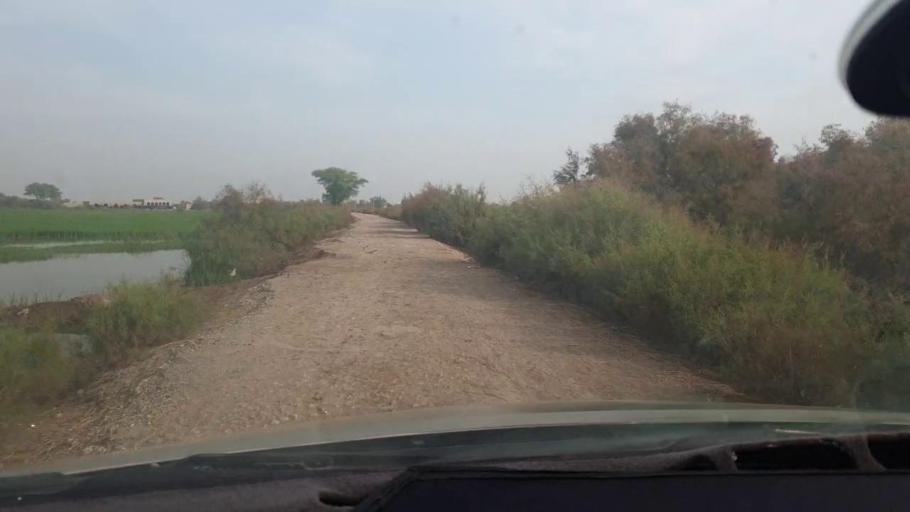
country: PK
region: Balochistan
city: Jhatpat
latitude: 28.3679
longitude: 68.4047
